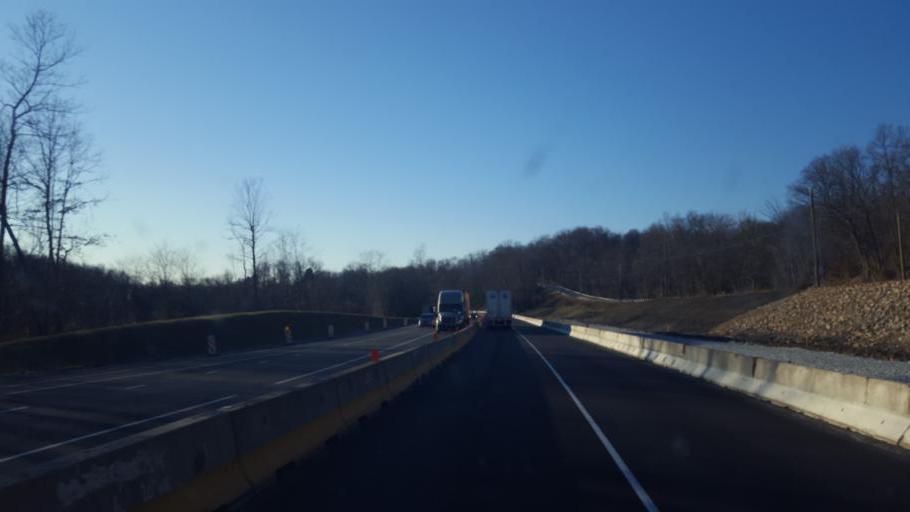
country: US
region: Pennsylvania
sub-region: Washington County
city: Bentleyville
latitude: 40.1275
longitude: -79.9605
